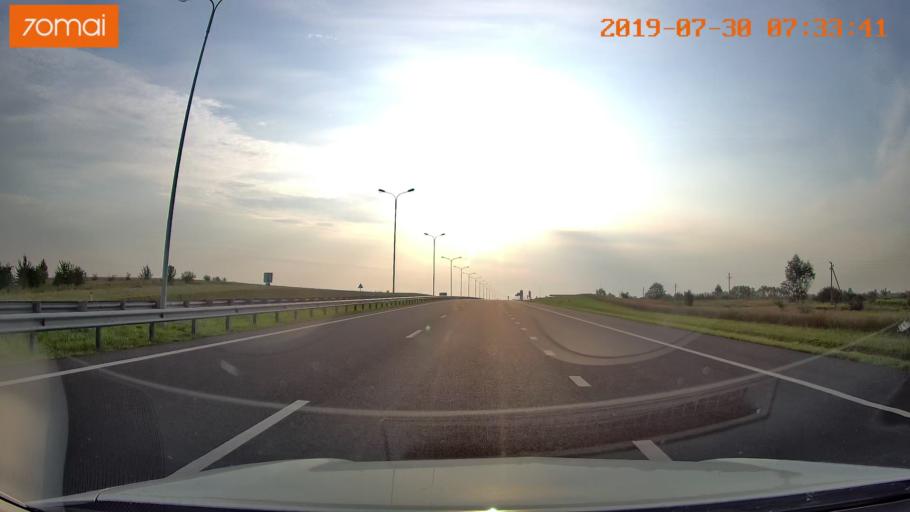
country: RU
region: Kaliningrad
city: Gvardeysk
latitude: 54.6703
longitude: 21.0515
